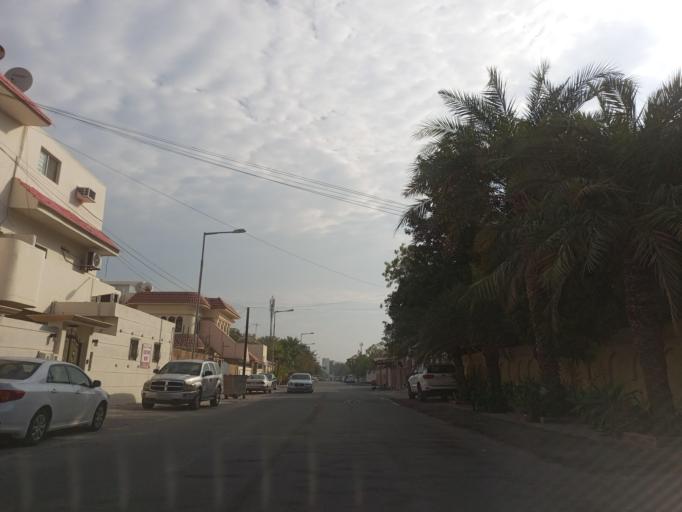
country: BH
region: Muharraq
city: Al Hadd
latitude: 26.2511
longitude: 50.6434
